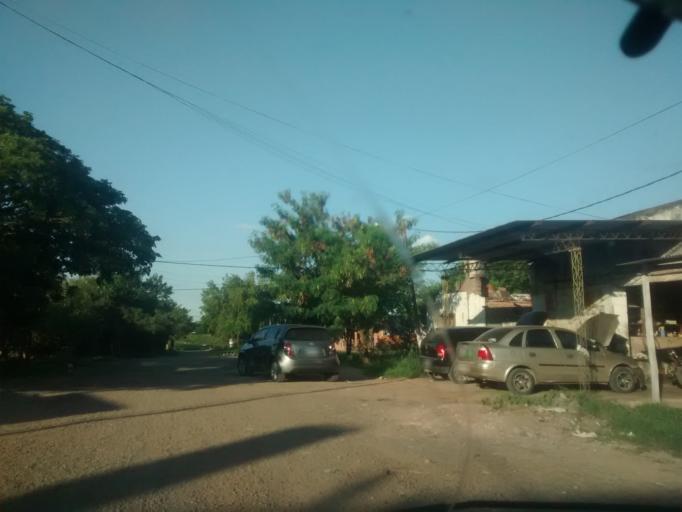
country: AR
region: Chaco
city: Fontana
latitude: -27.4395
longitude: -59.0108
